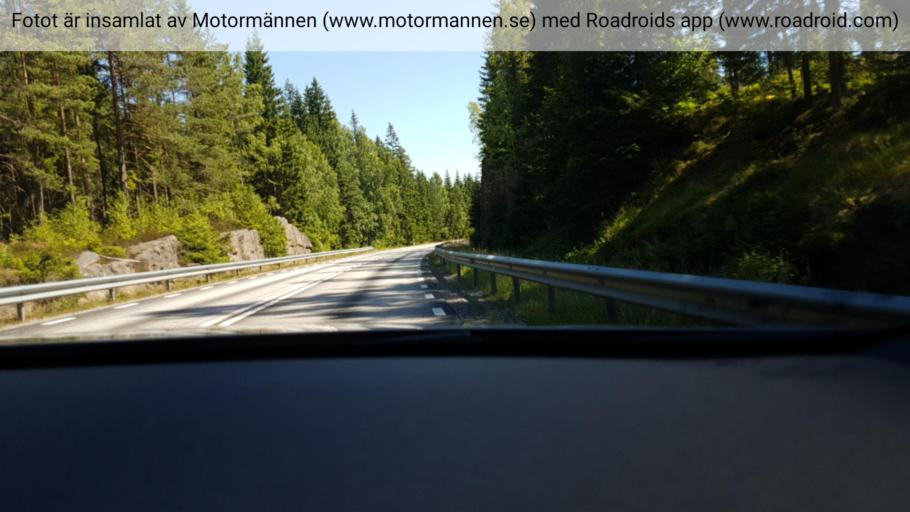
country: SE
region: Joenkoeping
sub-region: Gnosjo Kommun
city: Hillerstorp
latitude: 57.3308
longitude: 13.8139
